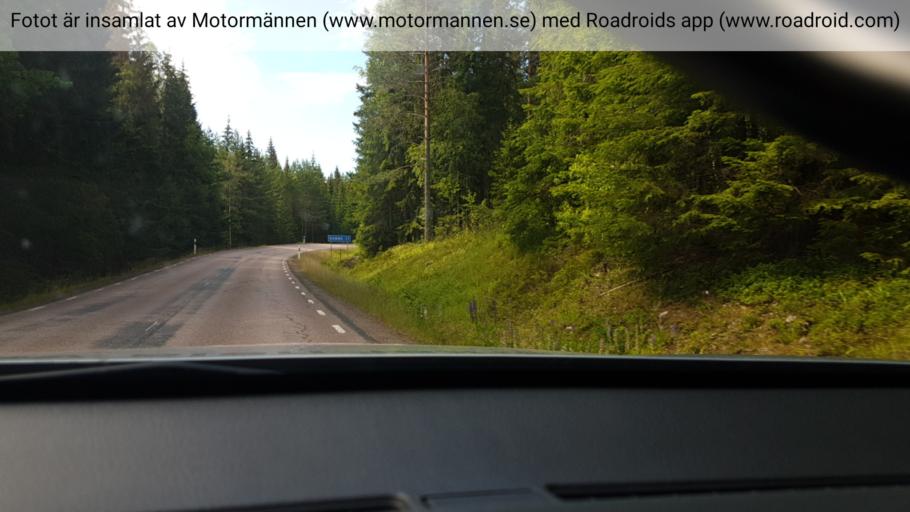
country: SE
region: Vaermland
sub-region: Sunne Kommun
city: Sunne
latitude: 59.8722
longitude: 13.3257
